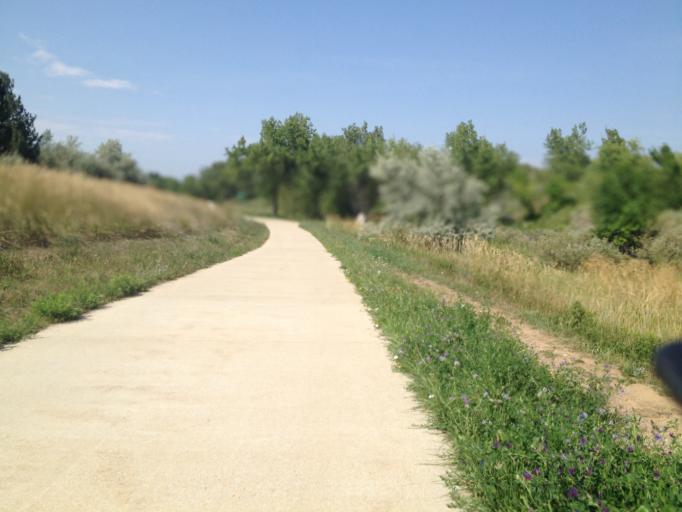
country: US
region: Colorado
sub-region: Boulder County
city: Boulder
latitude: 40.0214
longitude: -105.2162
